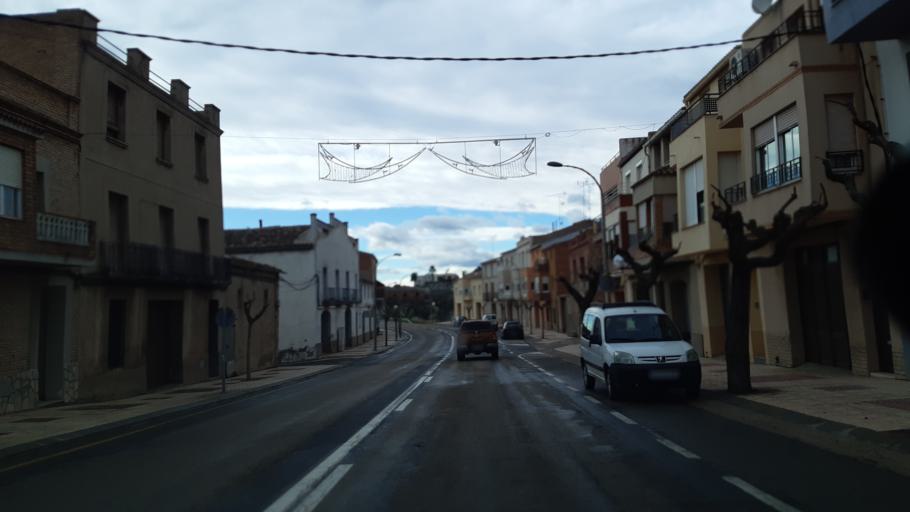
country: ES
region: Catalonia
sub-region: Provincia de Tarragona
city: Gandesa
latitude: 41.0759
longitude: 0.4725
